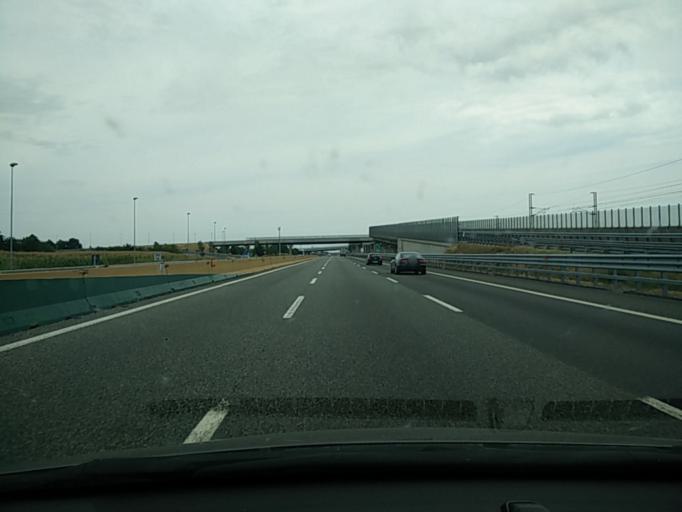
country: IT
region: Piedmont
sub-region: Provincia di Torino
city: Chivasso
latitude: 45.2202
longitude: 7.9154
